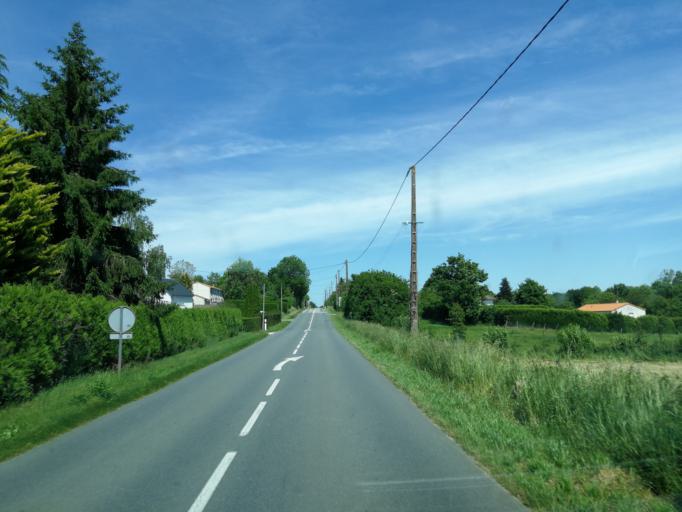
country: FR
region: Poitou-Charentes
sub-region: Departement des Deux-Sevres
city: Courlay
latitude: 46.7896
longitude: -0.6084
